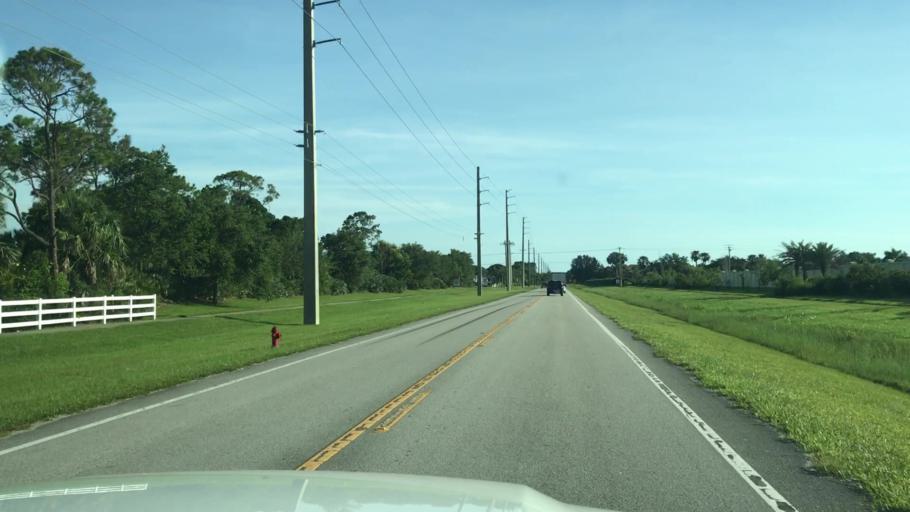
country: US
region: Florida
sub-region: Indian River County
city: Winter Beach
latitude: 27.7018
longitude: -80.4461
